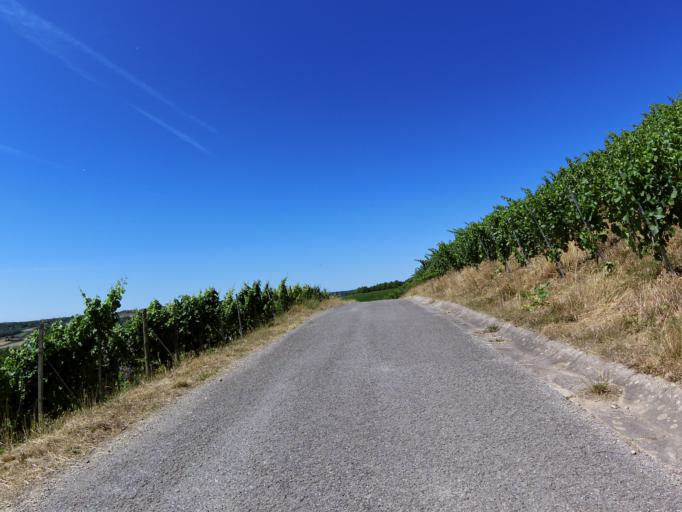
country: DE
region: Bavaria
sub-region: Regierungsbezirk Unterfranken
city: Randersacker
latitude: 49.7572
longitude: 9.9983
